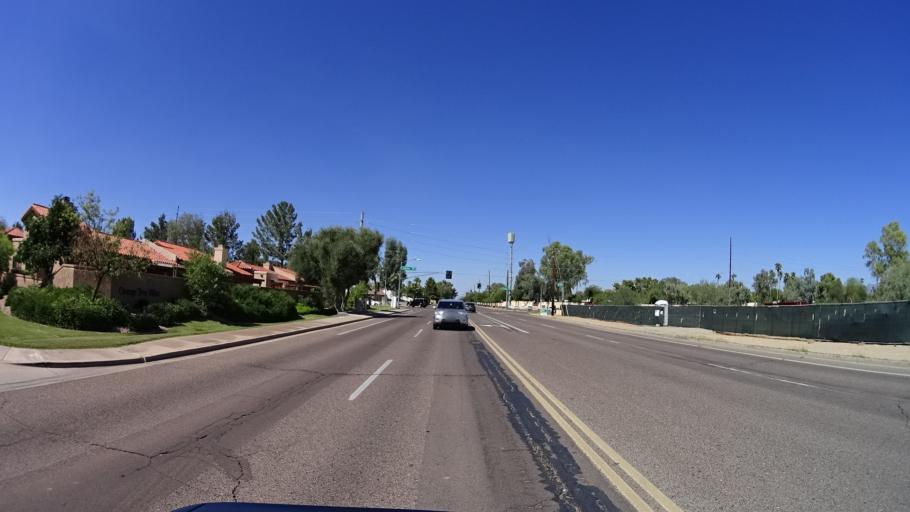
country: US
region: Arizona
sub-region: Maricopa County
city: Paradise Valley
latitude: 33.5965
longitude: -111.9606
